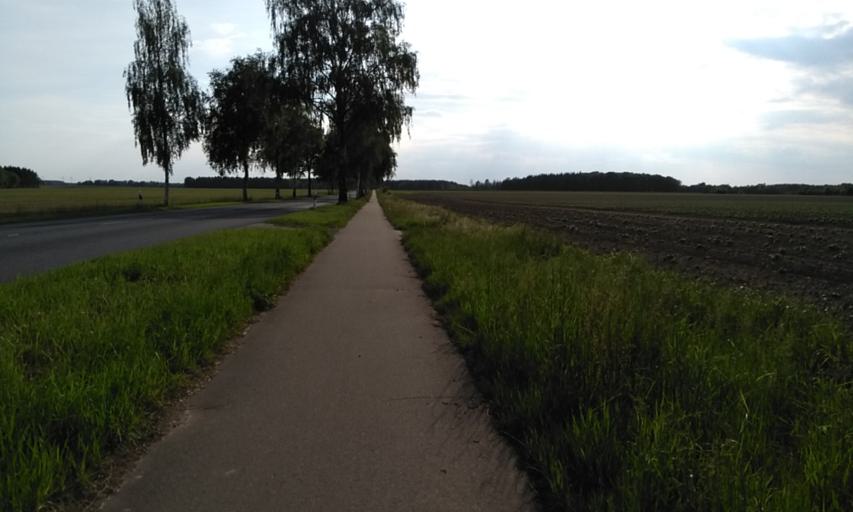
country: DE
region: Lower Saxony
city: Apensen
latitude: 53.4308
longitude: 9.5990
